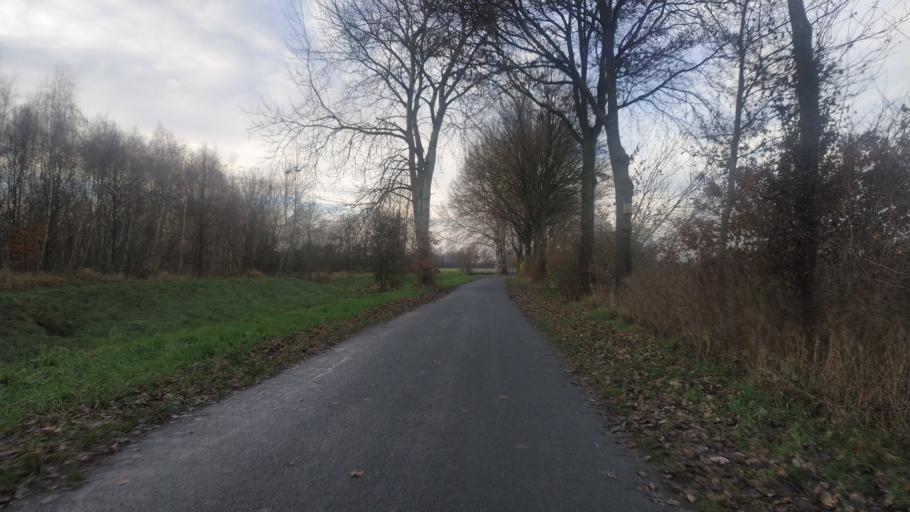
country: DE
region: North Rhine-Westphalia
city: Ibbenburen
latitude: 52.2806
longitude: 7.6826
